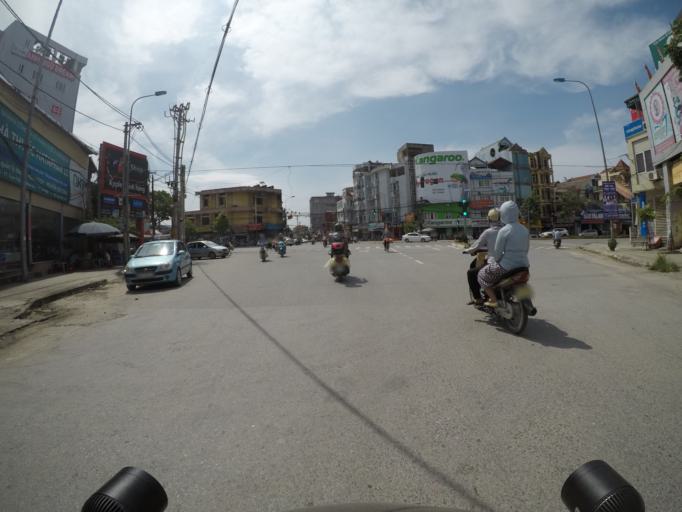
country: VN
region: Ha Noi
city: Troi
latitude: 21.0703
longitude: 105.7079
